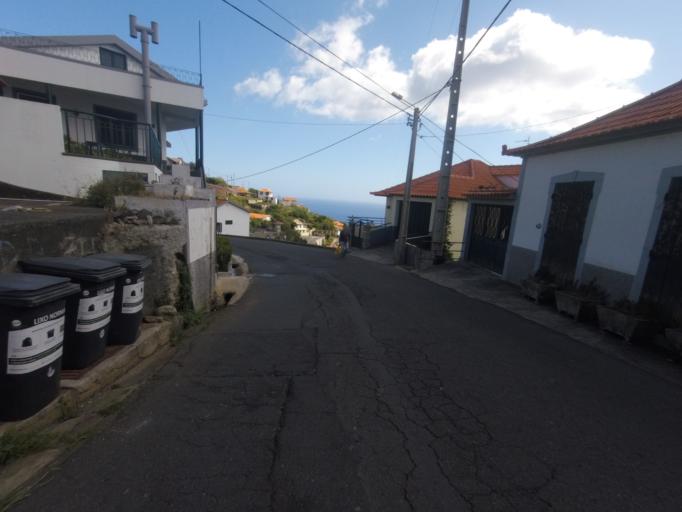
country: PT
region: Madeira
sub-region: Ribeira Brava
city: Campanario
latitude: 32.6690
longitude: -17.0504
